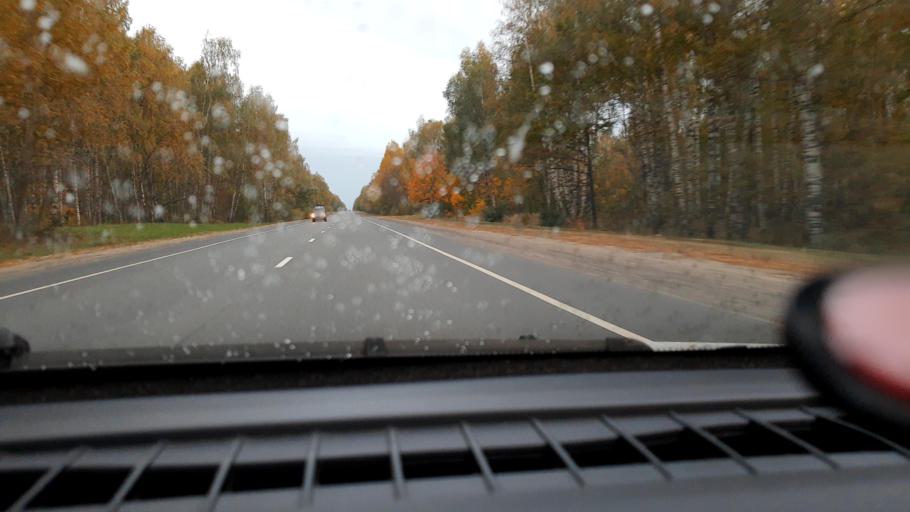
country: RU
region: Vladimir
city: Orgtrud
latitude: 56.2043
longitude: 40.7389
